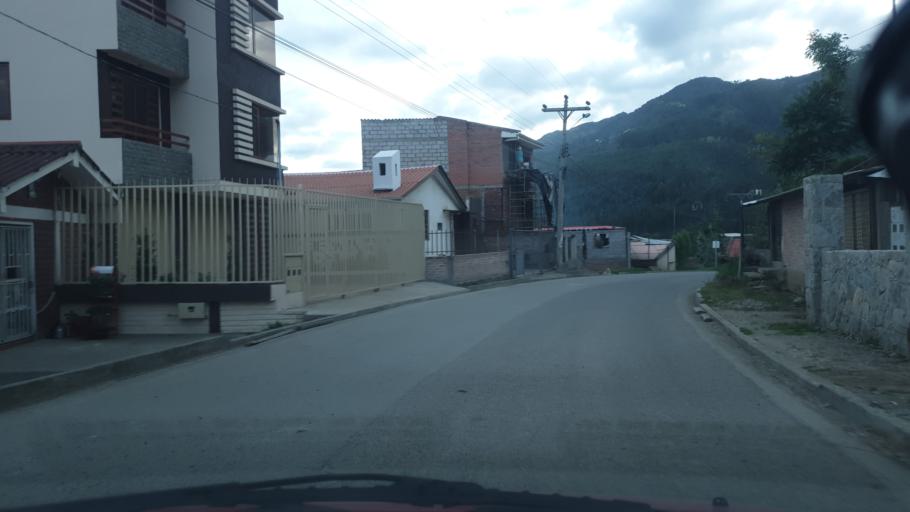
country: EC
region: Azuay
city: Cuenca
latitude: -2.8722
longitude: -79.0714
